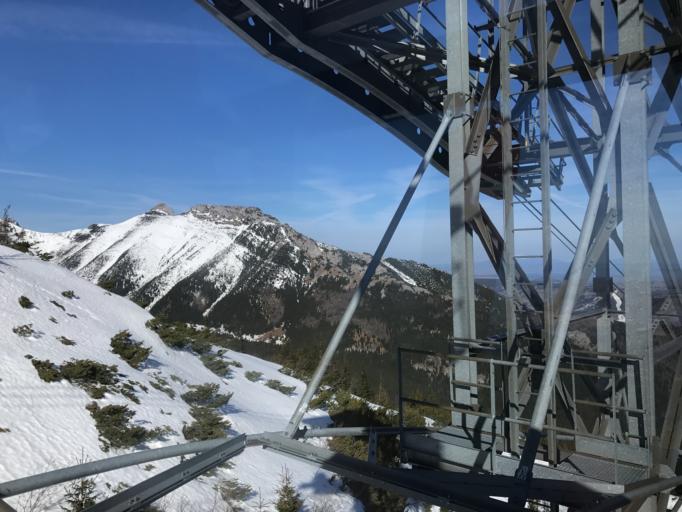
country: PL
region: Lesser Poland Voivodeship
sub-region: Powiat tatrzanski
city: Zakopane
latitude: 49.2441
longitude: 19.9771
